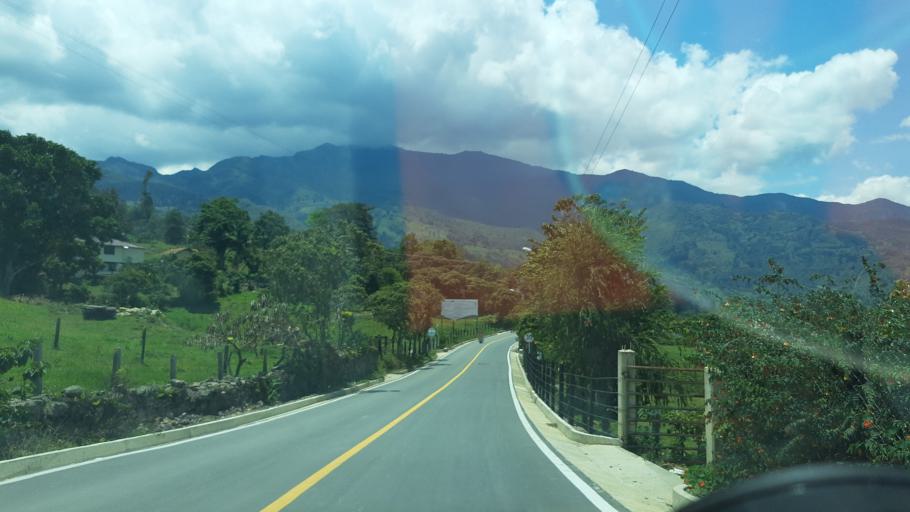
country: CO
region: Boyaca
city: Chinavita
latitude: 5.1369
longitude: -73.3943
